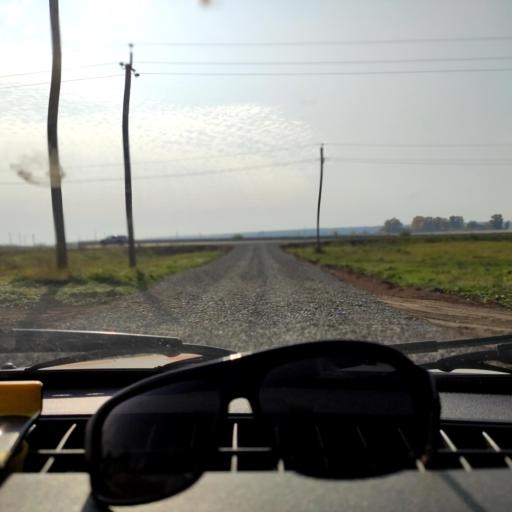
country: RU
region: Bashkortostan
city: Mikhaylovka
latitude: 54.8889
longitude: 55.9014
